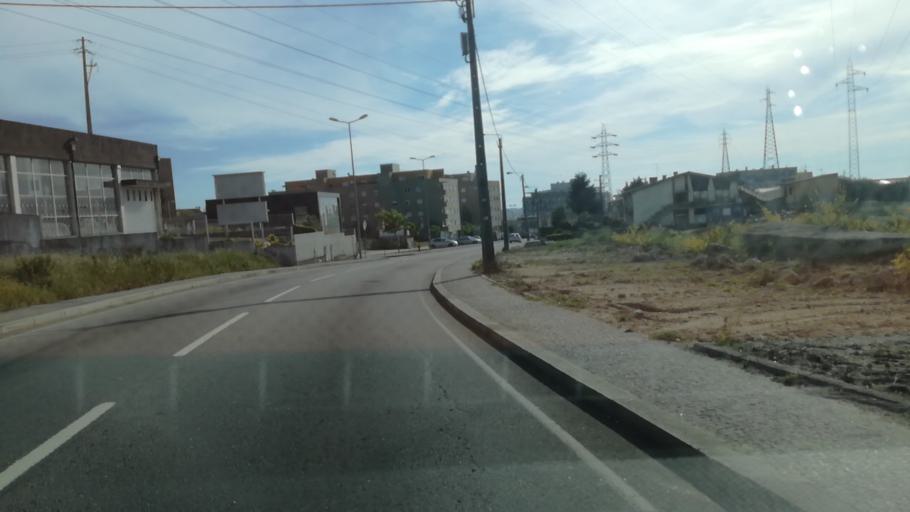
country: PT
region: Porto
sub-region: Maia
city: Nogueira
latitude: 41.2302
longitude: -8.5761
